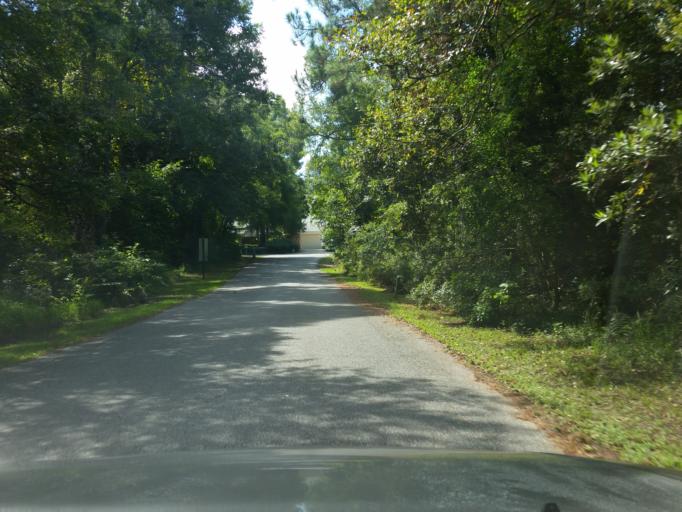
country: US
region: Alabama
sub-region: Baldwin County
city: Orange Beach
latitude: 30.3161
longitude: -87.4853
